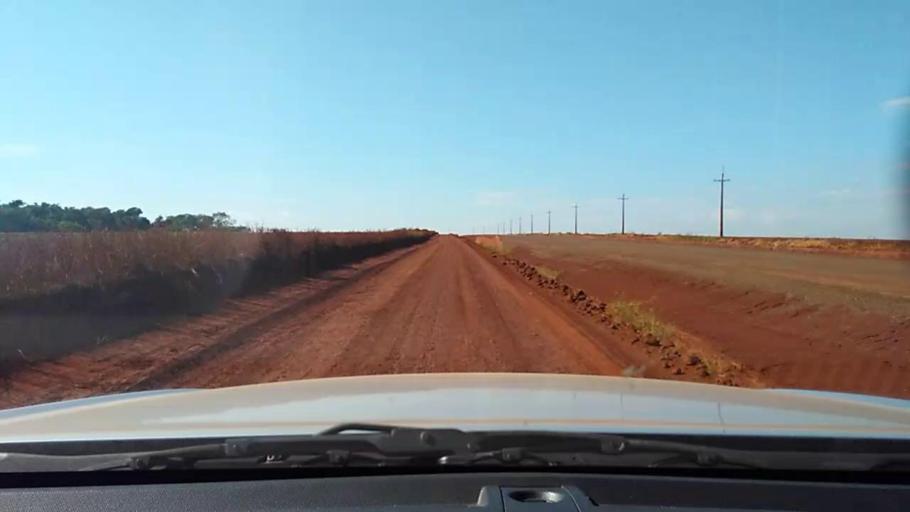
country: PY
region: Alto Parana
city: Naranjal
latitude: -25.9119
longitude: -55.4411
